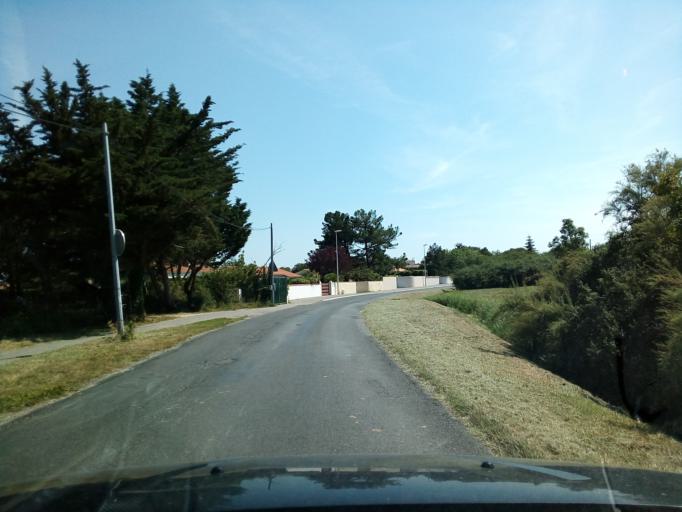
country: FR
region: Poitou-Charentes
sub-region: Departement de la Charente-Maritime
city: Boyard-Ville
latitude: 45.9755
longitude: -1.2983
